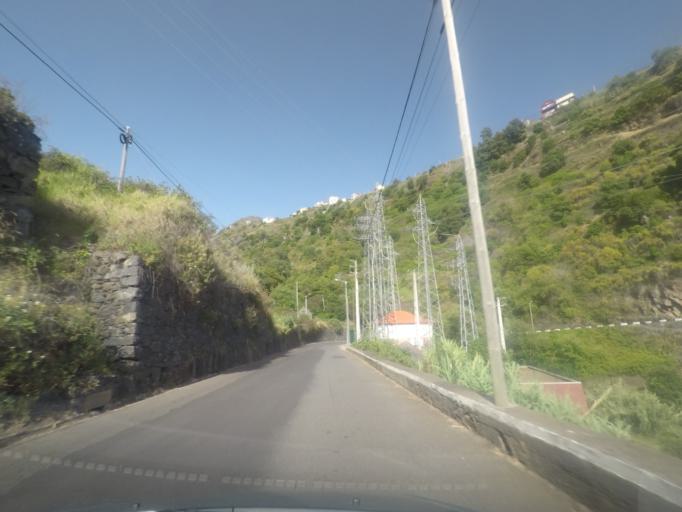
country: PT
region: Madeira
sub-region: Calheta
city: Arco da Calheta
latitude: 32.7304
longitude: -17.1644
